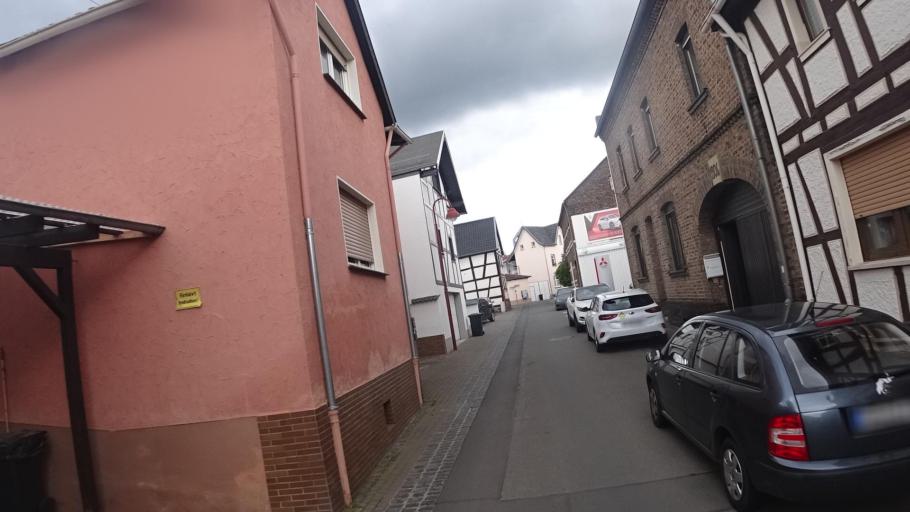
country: DE
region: Rheinland-Pfalz
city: Bad Neuenahr-Ahrweiler
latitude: 50.5540
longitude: 7.1080
